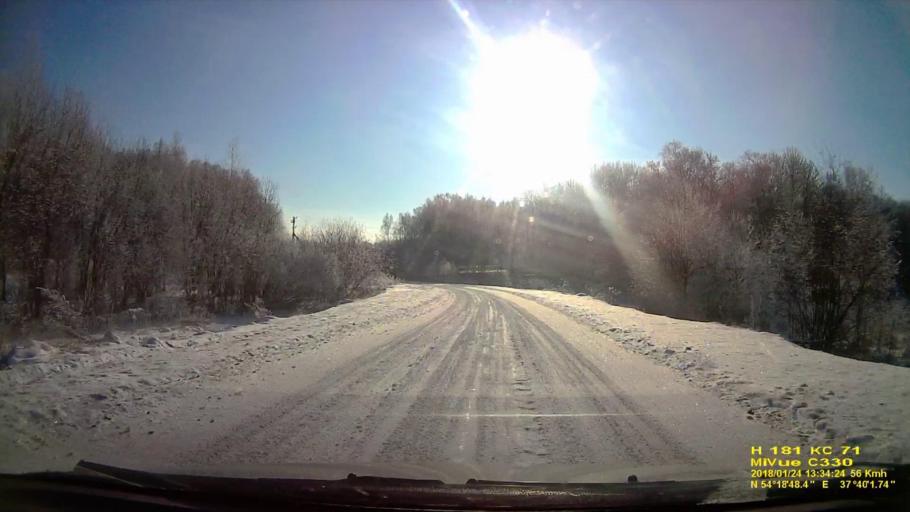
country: RU
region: Tula
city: Revyakino
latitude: 54.3133
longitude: 37.6671
